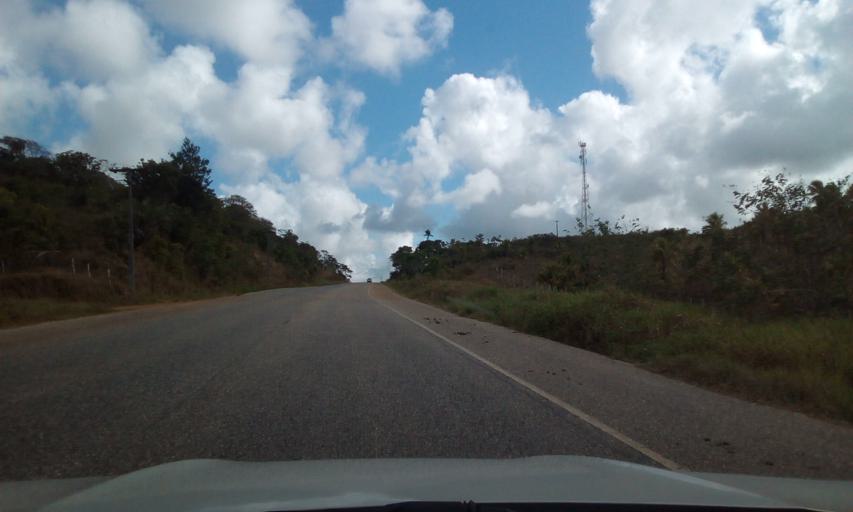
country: BR
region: Sergipe
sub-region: Estancia
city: Estancia
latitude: -11.3608
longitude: -37.4540
